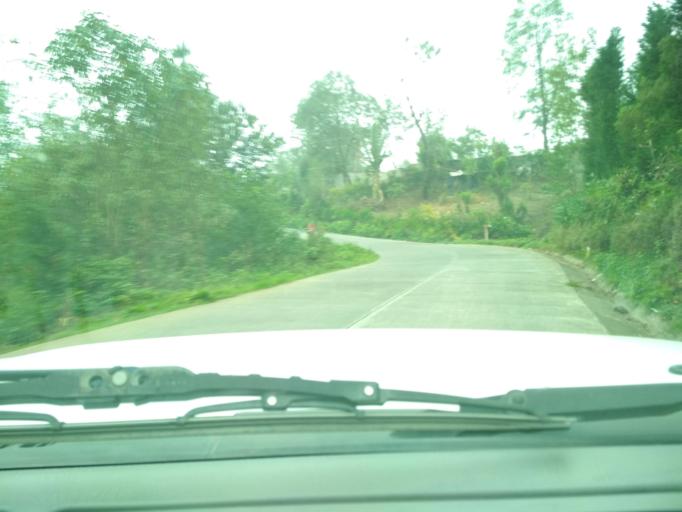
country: MX
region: Veracruz
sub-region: La Perla
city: Chilapa
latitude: 18.9733
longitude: -97.1642
